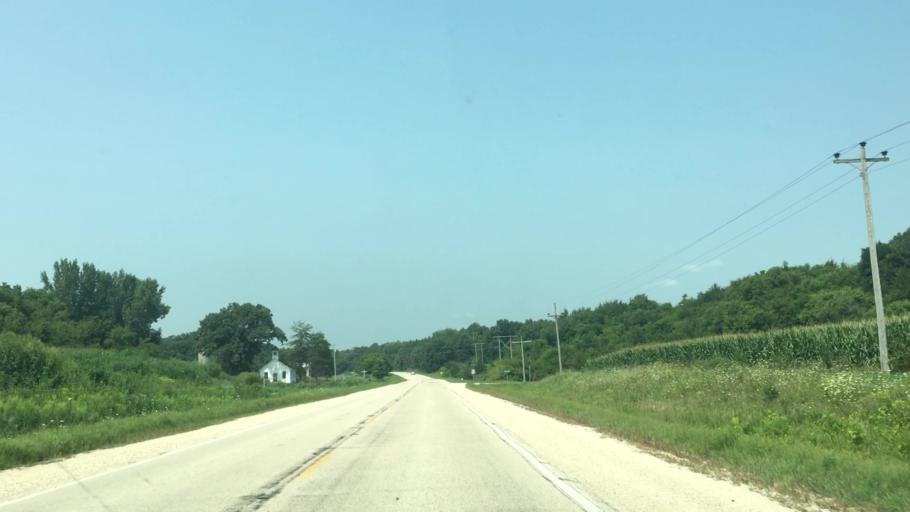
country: US
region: Iowa
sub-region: Fayette County
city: West Union
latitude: 43.0685
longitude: -91.8388
